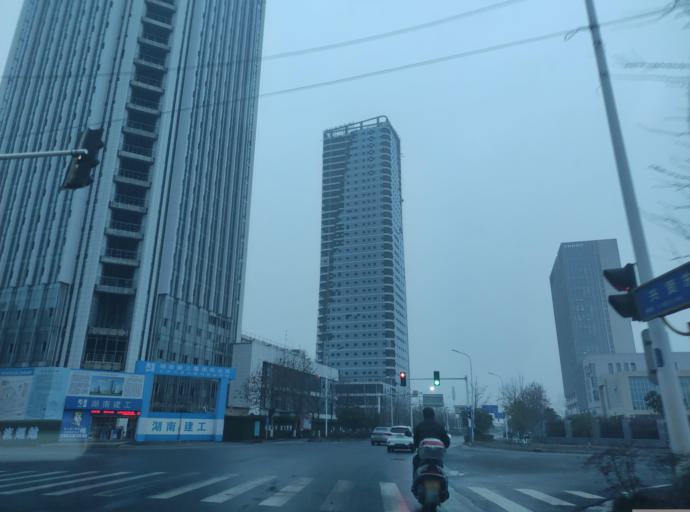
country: CN
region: Jiangxi Sheng
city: Pingxiang
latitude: 27.6654
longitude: 113.8789
